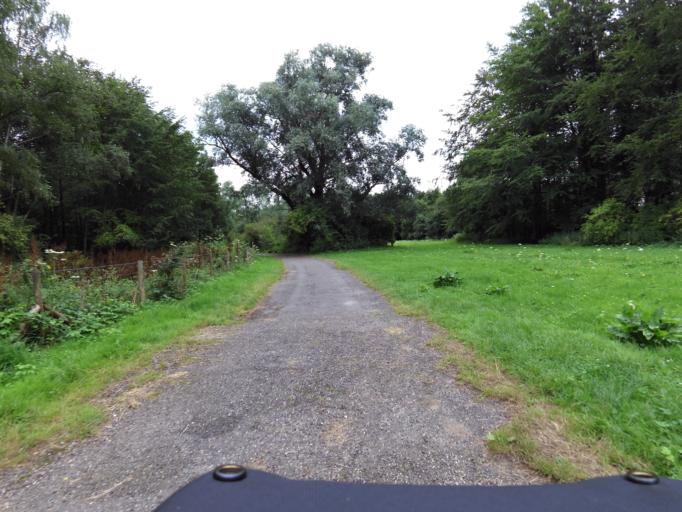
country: NL
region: South Holland
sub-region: Gemeente Spijkenisse
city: Spijkenisse
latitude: 51.8679
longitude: 4.3392
